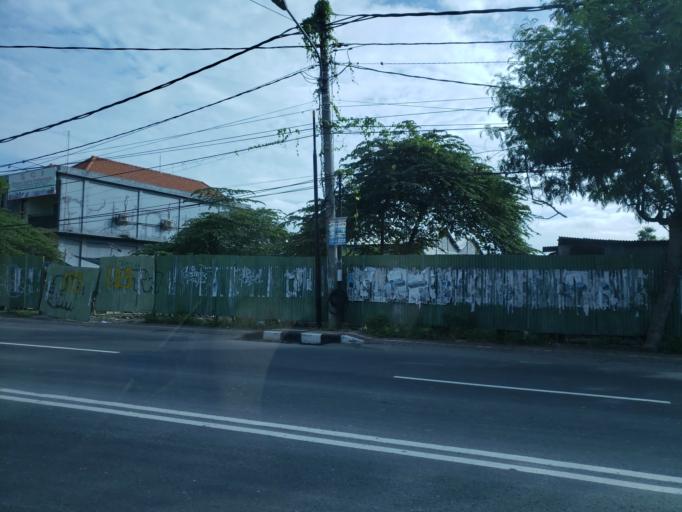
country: ID
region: Bali
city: Denpasar
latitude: -8.6765
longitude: 115.1905
